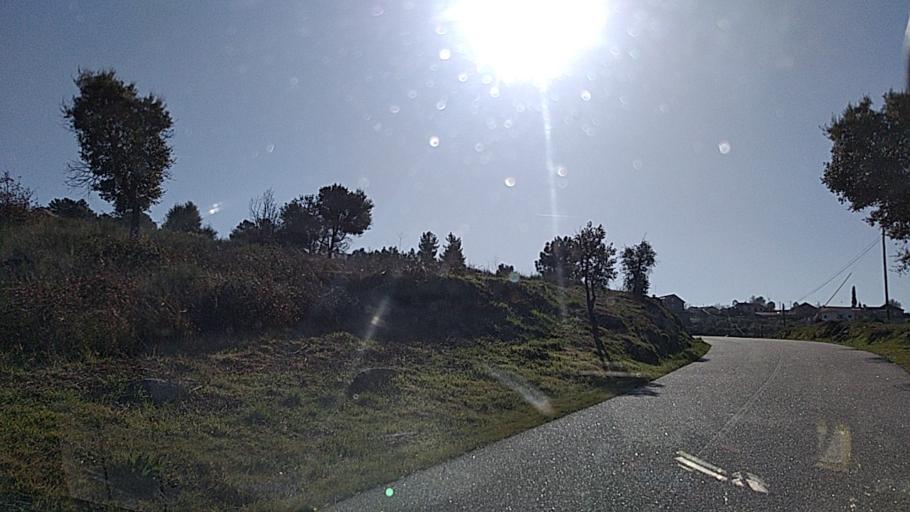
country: PT
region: Guarda
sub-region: Celorico da Beira
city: Celorico da Beira
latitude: 40.6921
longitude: -7.4460
